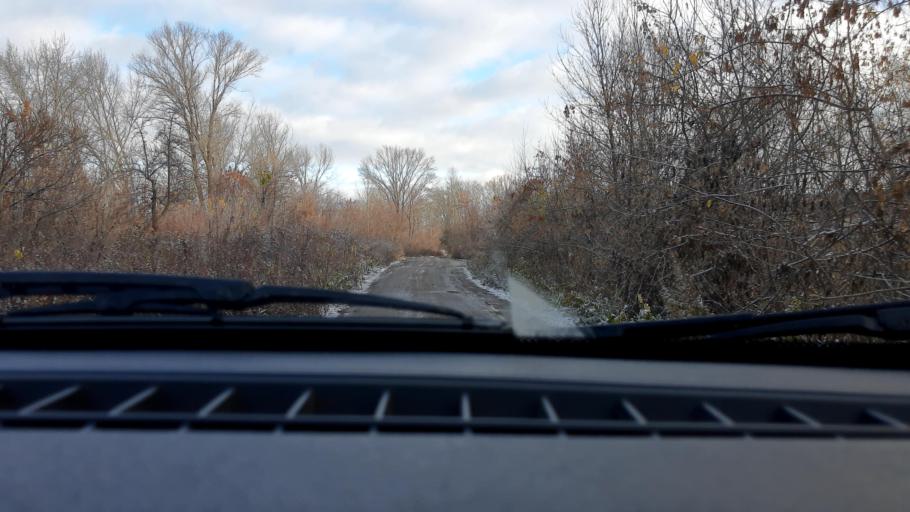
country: RU
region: Bashkortostan
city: Ufa
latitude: 54.7597
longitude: 55.9724
